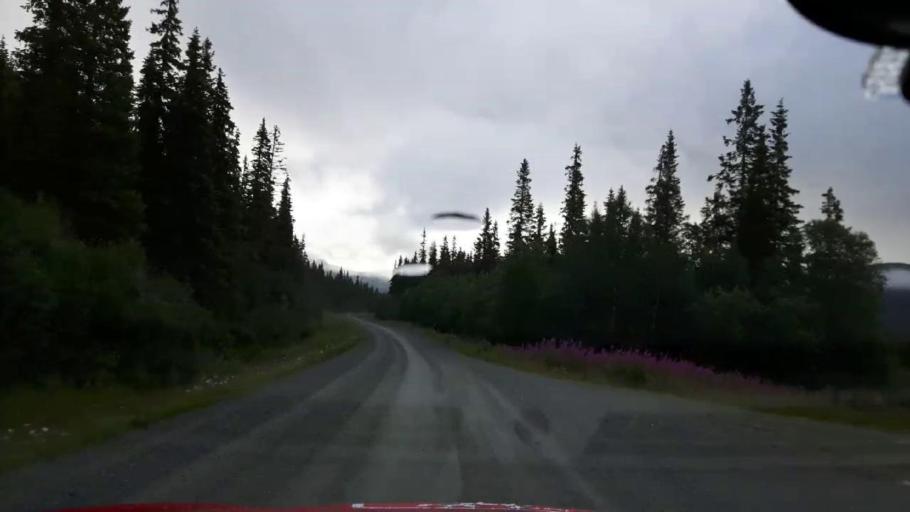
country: NO
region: Nordland
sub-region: Hattfjelldal
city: Hattfjelldal
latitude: 64.8829
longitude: 14.7739
